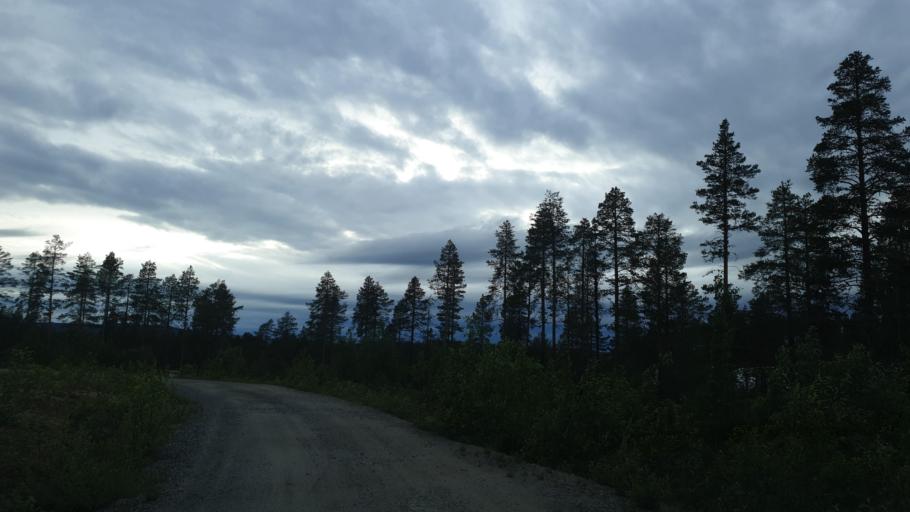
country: SE
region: Norrbotten
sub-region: Jokkmokks Kommun
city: Jokkmokk
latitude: 66.1532
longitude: 19.9950
